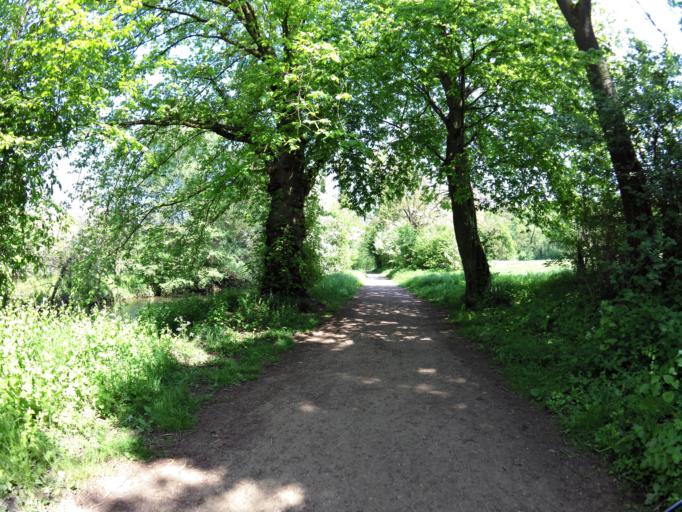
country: NL
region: Limburg
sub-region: Valkenburg aan de Geul
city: Valkenburg
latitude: 50.8605
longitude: 5.8413
